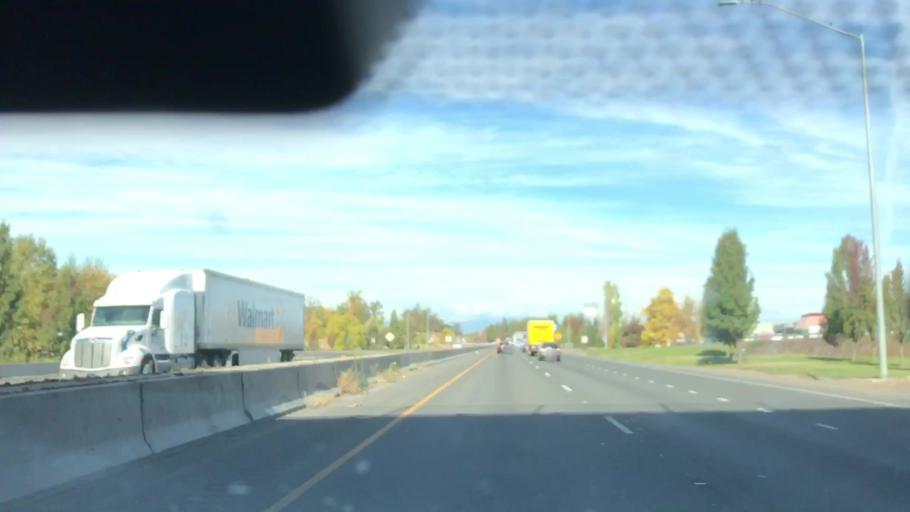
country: US
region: Oregon
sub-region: Jackson County
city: Medford
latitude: 42.3505
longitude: -122.8766
